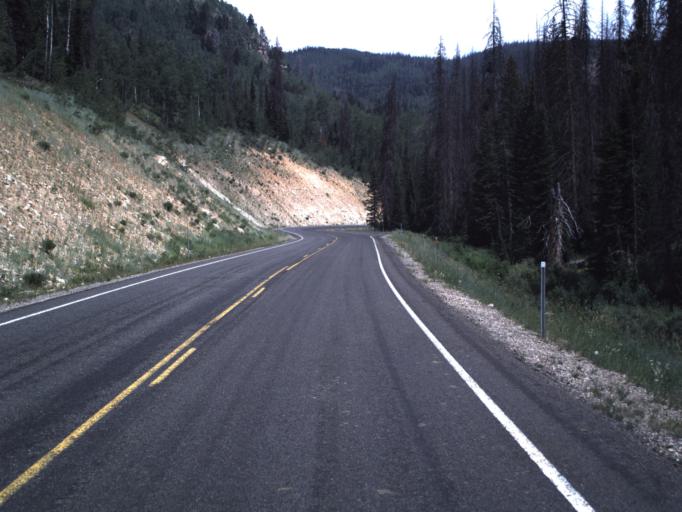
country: US
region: Utah
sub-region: Summit County
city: Francis
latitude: 40.4943
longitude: -110.9808
